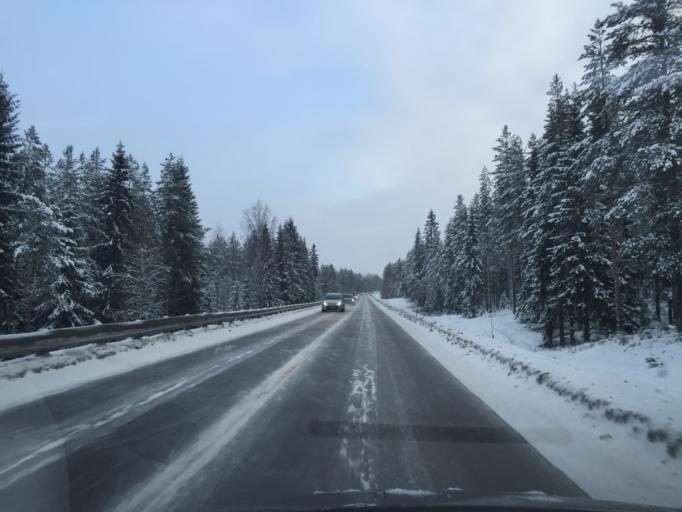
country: NO
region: Hedmark
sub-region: Elverum
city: Elverum
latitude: 60.9535
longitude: 11.7015
